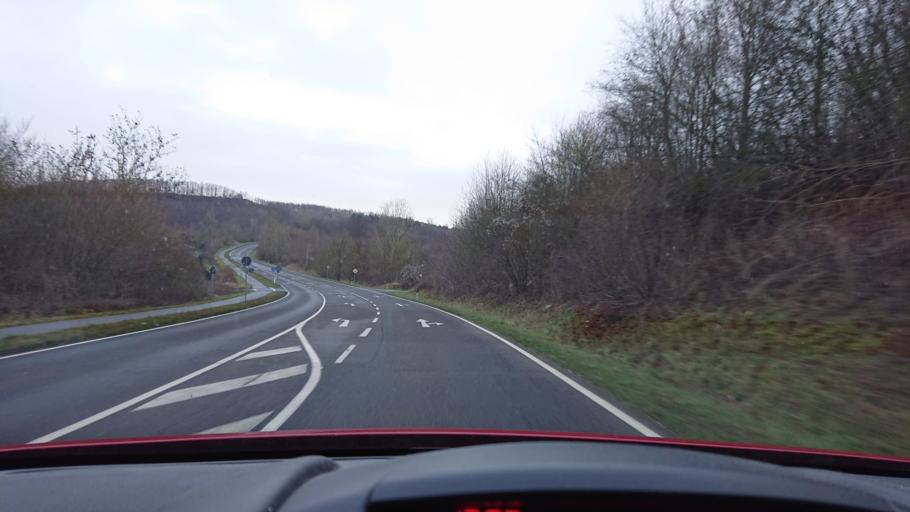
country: DE
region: North Rhine-Westphalia
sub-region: Regierungsbezirk Koln
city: Bergheim
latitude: 50.9622
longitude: 6.6855
